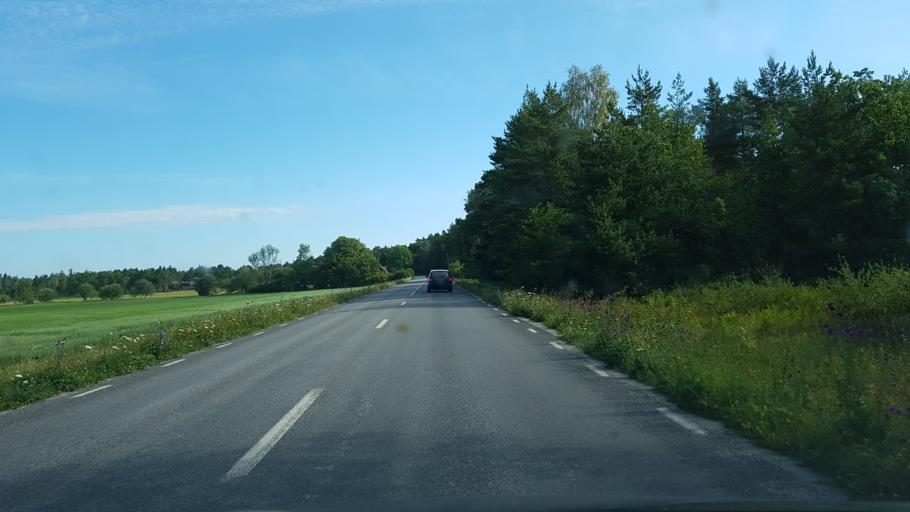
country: SE
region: Gotland
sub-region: Gotland
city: Visby
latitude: 57.7794
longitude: 18.4537
